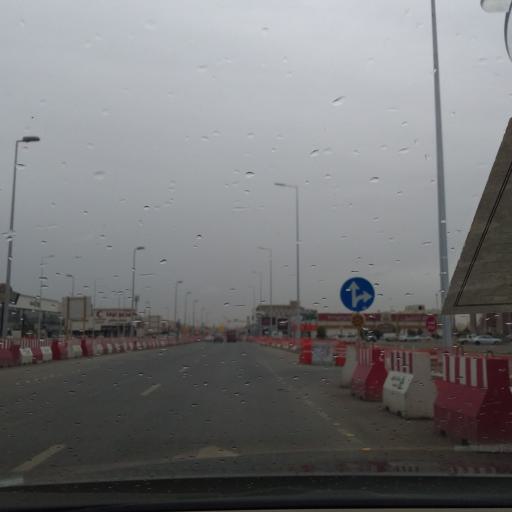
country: SA
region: Ar Riyad
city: Riyadh
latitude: 24.7358
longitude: 46.7831
